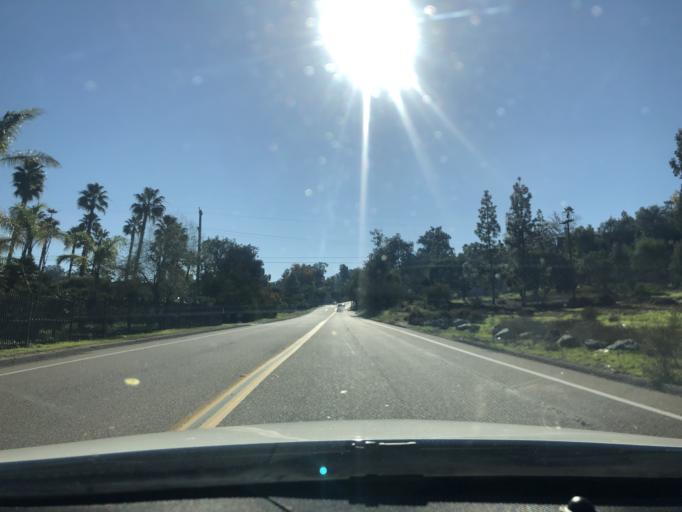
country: US
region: California
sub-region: San Diego County
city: El Cajon
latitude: 32.7778
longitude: -116.9439
